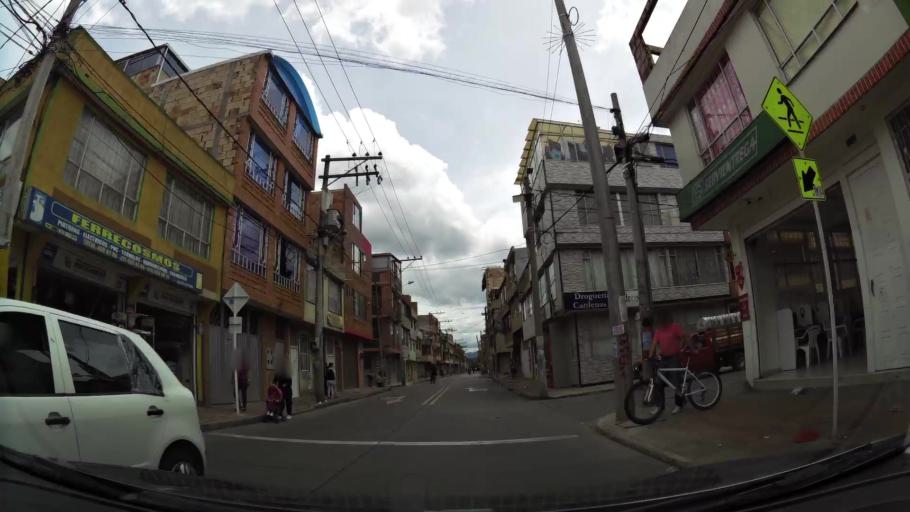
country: CO
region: Cundinamarca
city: Funza
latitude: 4.6978
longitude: -74.1249
